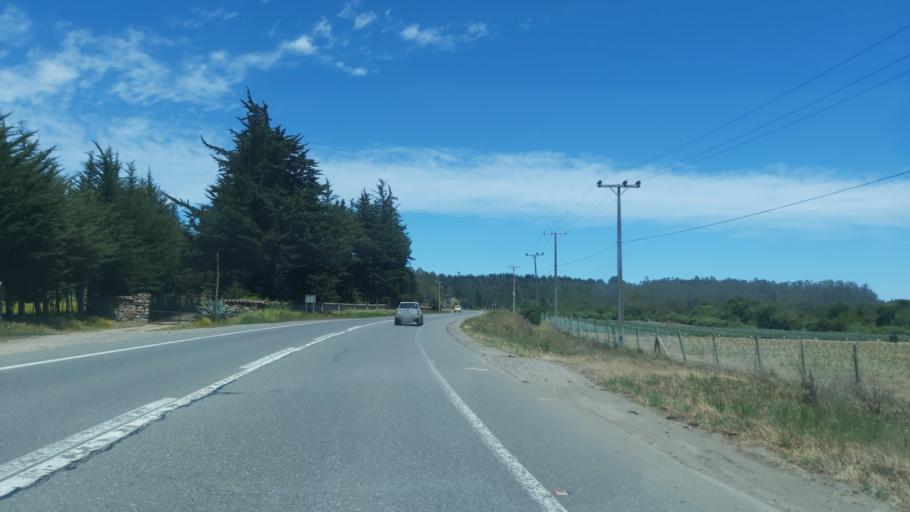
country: CL
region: Maule
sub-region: Provincia de Talca
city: Constitucion
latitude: -35.3117
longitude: -72.3822
